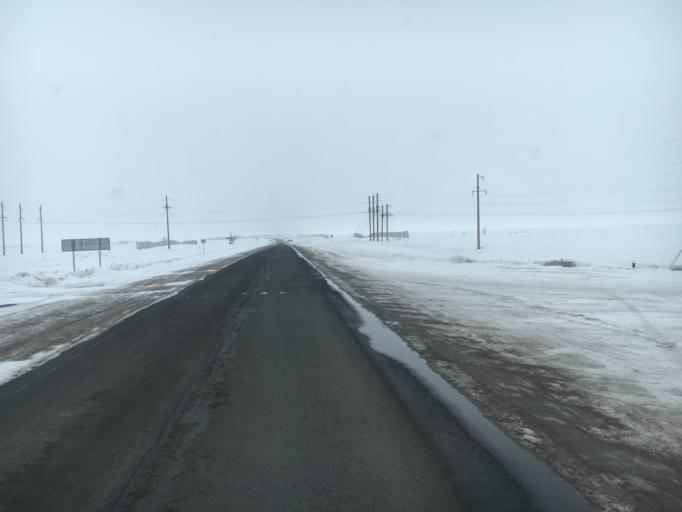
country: KZ
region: Batys Qazaqstan
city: Fedorovka
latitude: 50.7622
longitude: 51.9117
